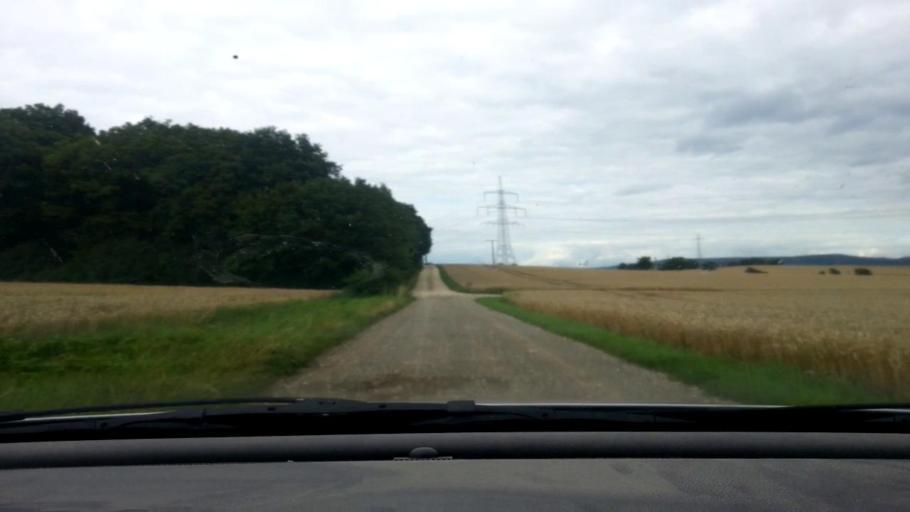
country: DE
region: Bavaria
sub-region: Upper Franconia
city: Memmelsdorf
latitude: 49.9479
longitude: 10.9522
